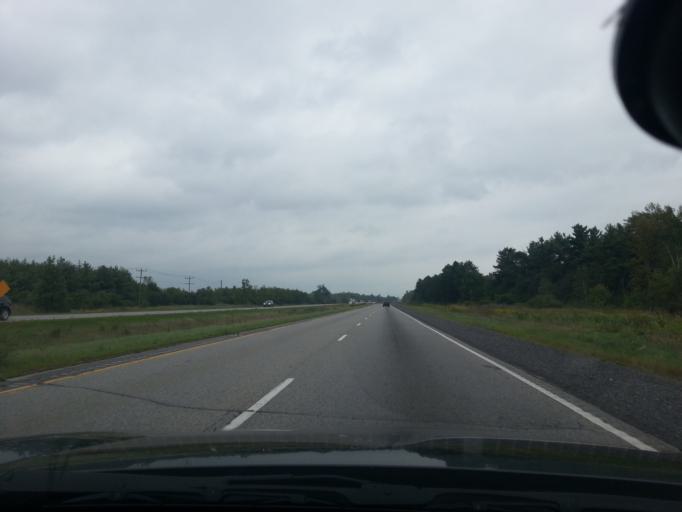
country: CA
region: Ontario
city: Prescott
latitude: 44.7045
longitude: -75.5643
